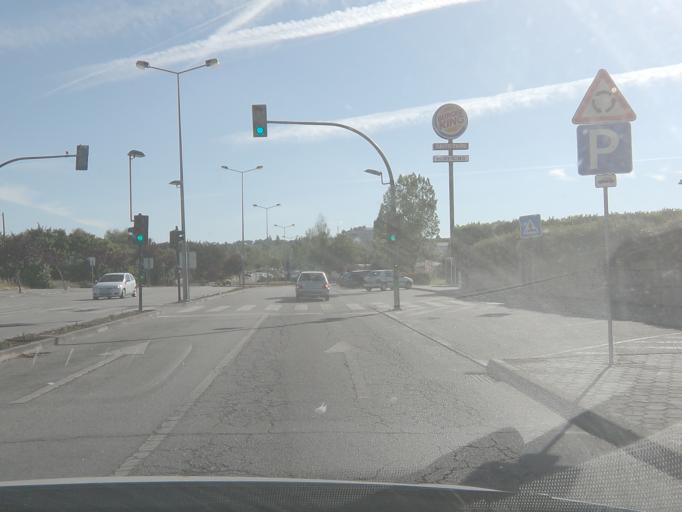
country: PT
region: Viseu
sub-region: Viseu
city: Abraveses
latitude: 40.6730
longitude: -7.9155
